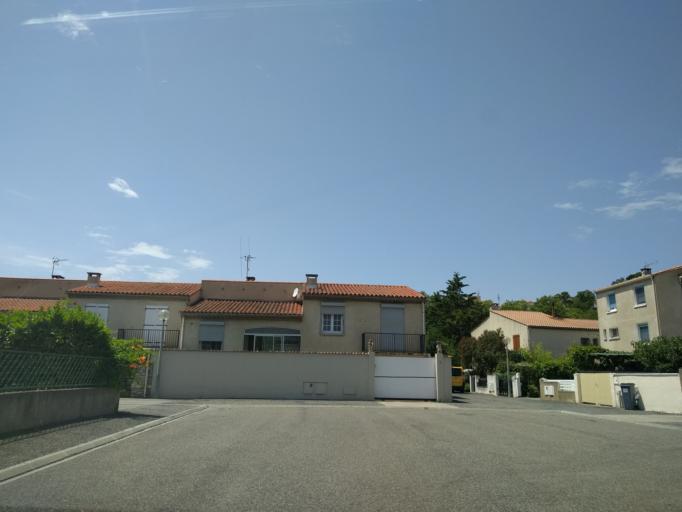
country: FR
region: Languedoc-Roussillon
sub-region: Departement de l'Aude
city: Carcassonne
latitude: 43.2209
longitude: 2.3583
